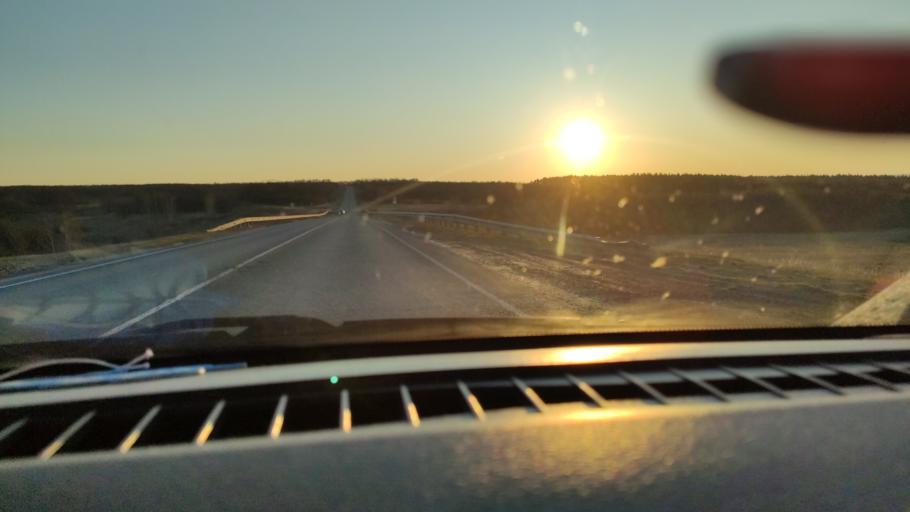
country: RU
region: Saratov
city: Sinodskoye
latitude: 51.9297
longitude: 46.5759
